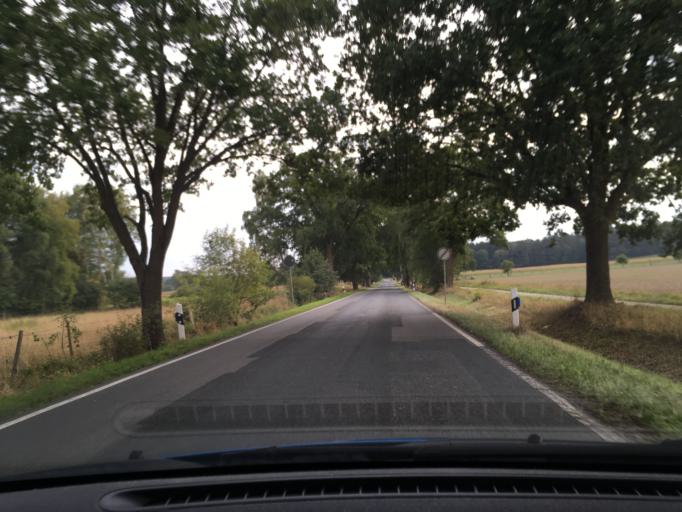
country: DE
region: Lower Saxony
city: Asendorf
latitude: 53.2819
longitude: 9.9758
